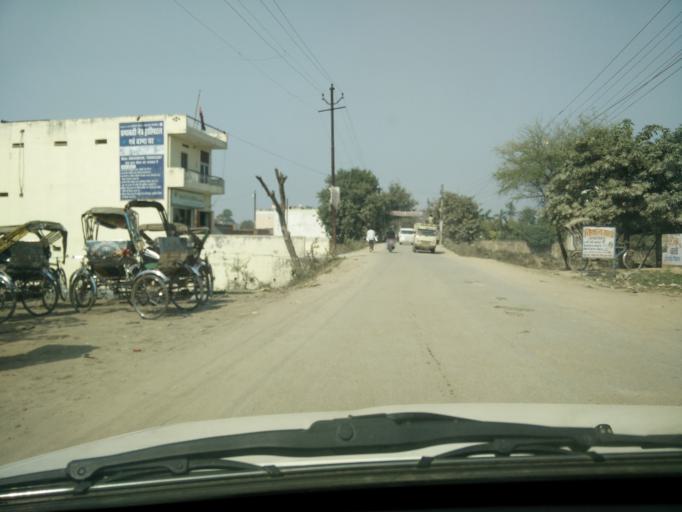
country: IN
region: Uttar Pradesh
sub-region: Varanasi
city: Ramnagar
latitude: 25.2663
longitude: 83.0161
